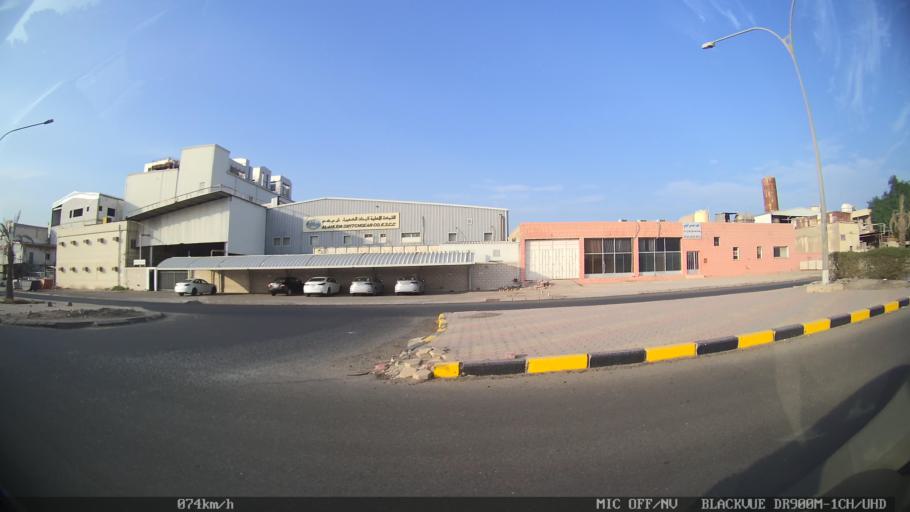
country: KW
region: Mubarak al Kabir
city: Sabah as Salim
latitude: 29.2237
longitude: 48.0135
